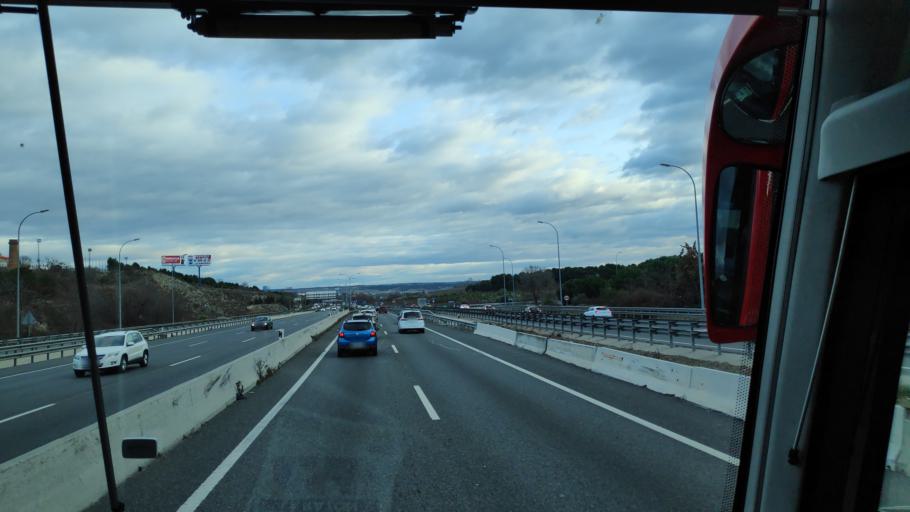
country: ES
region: Madrid
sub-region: Provincia de Madrid
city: Vaciamadrid
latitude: 40.3534
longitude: -3.5519
